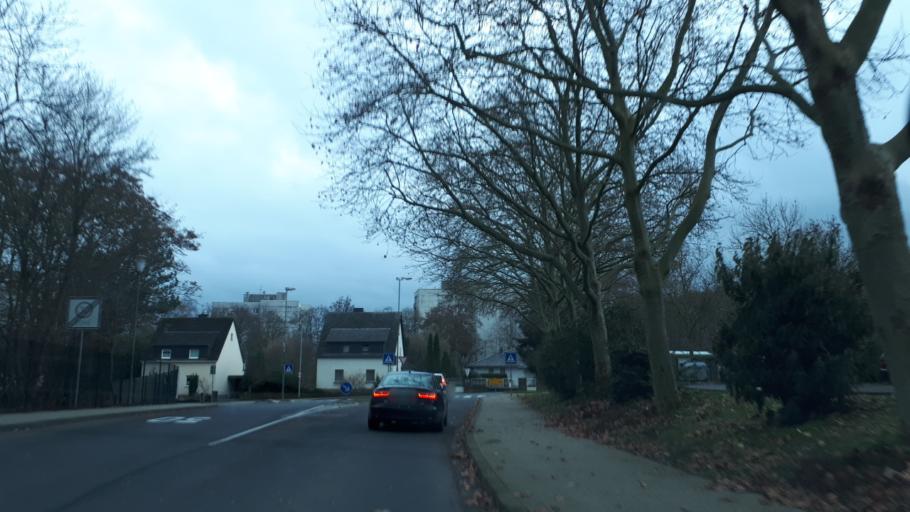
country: DE
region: Rheinland-Pfalz
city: Andernach
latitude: 50.4274
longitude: 7.3963
